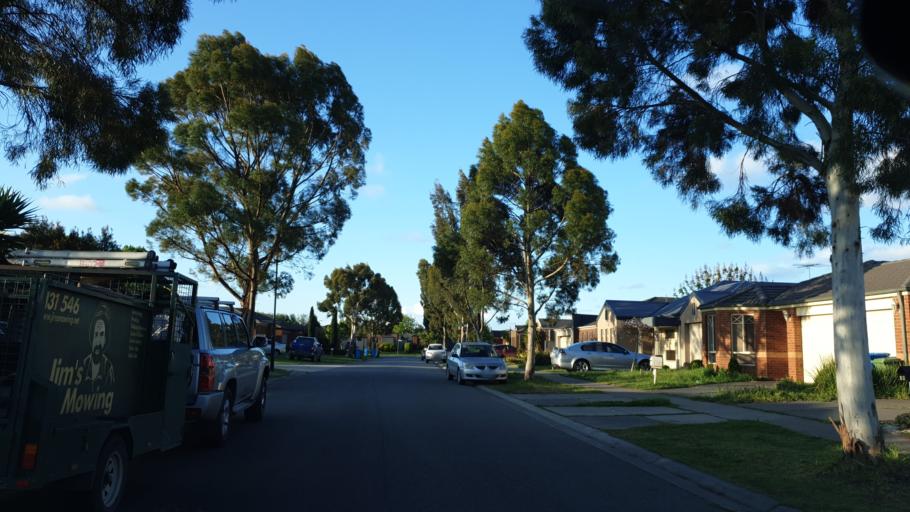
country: AU
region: Victoria
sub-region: Casey
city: Cranbourne East
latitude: -38.1111
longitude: 145.3042
